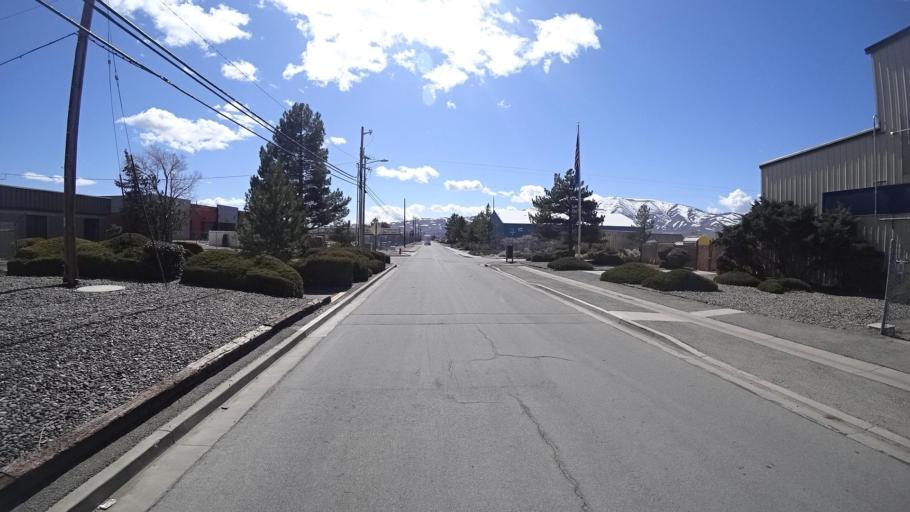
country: US
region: Nevada
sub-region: Washoe County
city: Lemmon Valley
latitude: 39.6573
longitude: -119.8830
